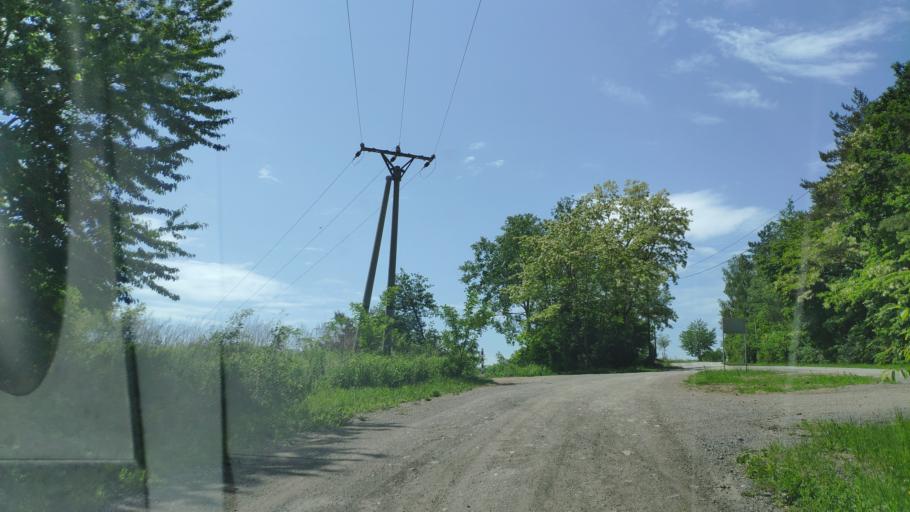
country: SK
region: Kosicky
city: Medzev
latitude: 48.7159
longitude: 20.9836
